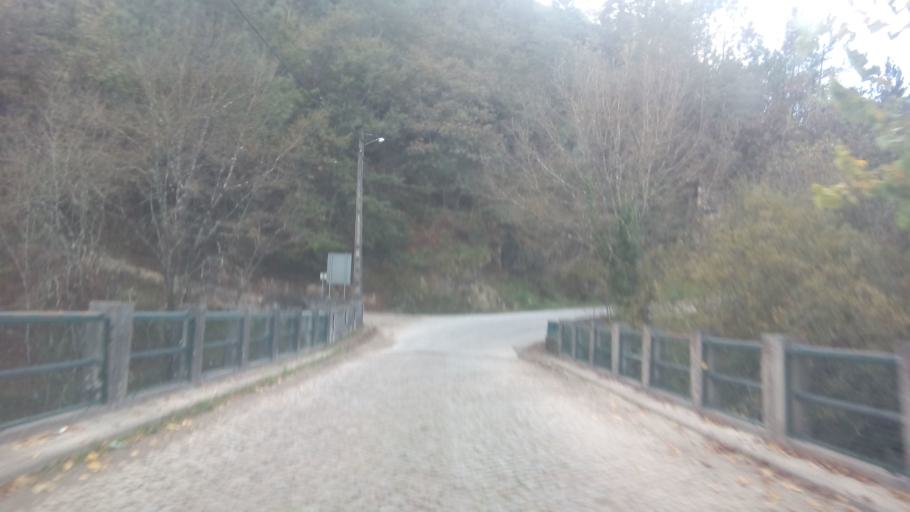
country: PT
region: Porto
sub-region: Amarante
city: Amarante
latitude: 41.2662
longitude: -8.0075
